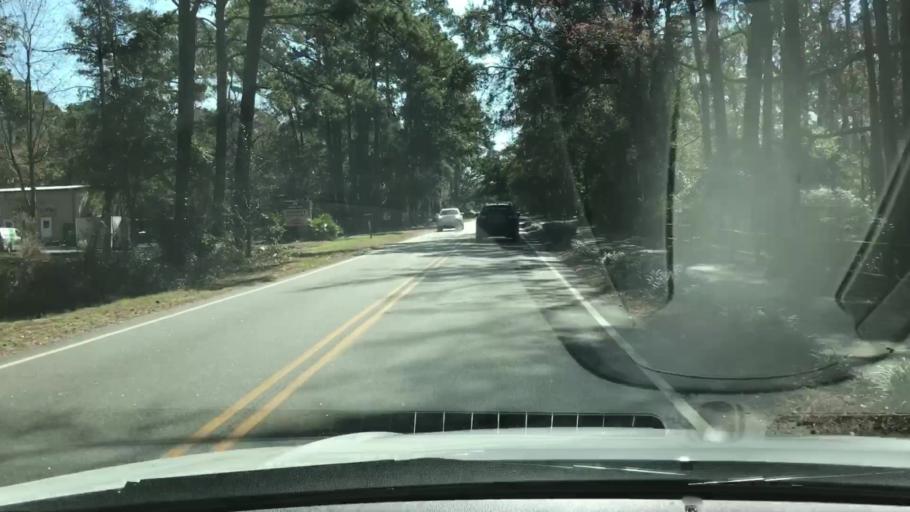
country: US
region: South Carolina
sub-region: Beaufort County
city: Hilton Head Island
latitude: 32.2209
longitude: -80.7049
